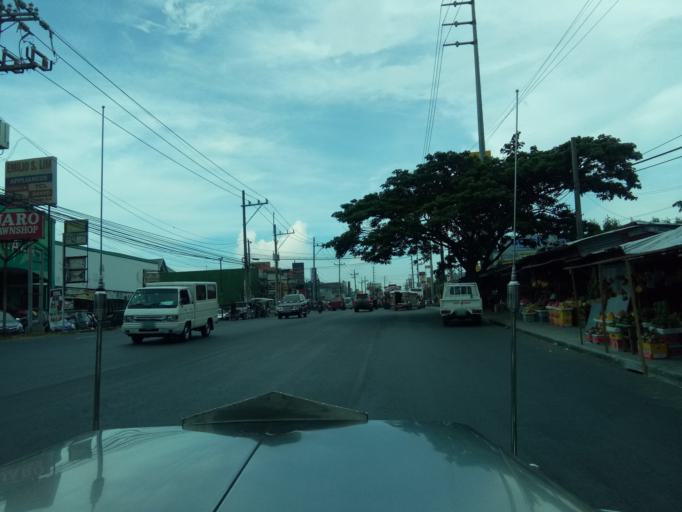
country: PH
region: Calabarzon
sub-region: Province of Cavite
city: Manggahan
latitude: 14.2918
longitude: 120.9076
